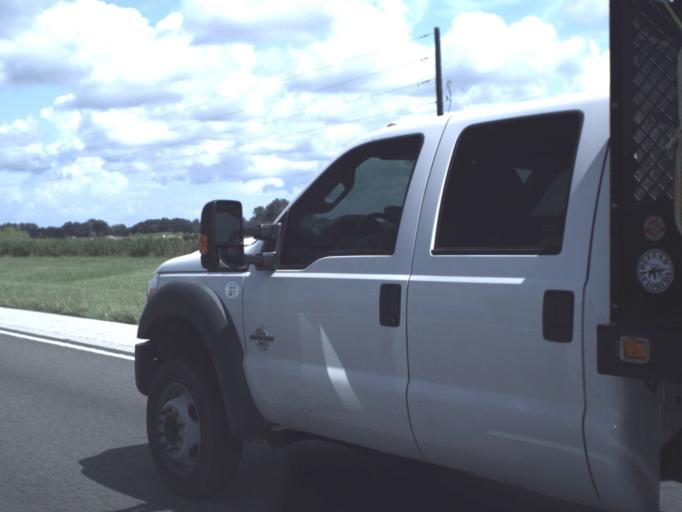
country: US
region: Florida
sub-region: Manatee County
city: Ellenton
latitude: 27.5670
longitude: -82.5134
